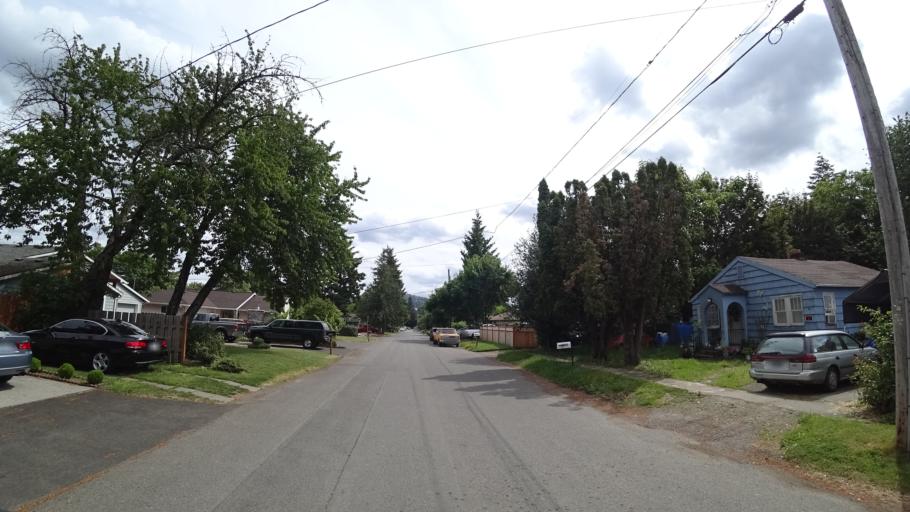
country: US
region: Oregon
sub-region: Multnomah County
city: Lents
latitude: 45.4853
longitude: -122.5525
